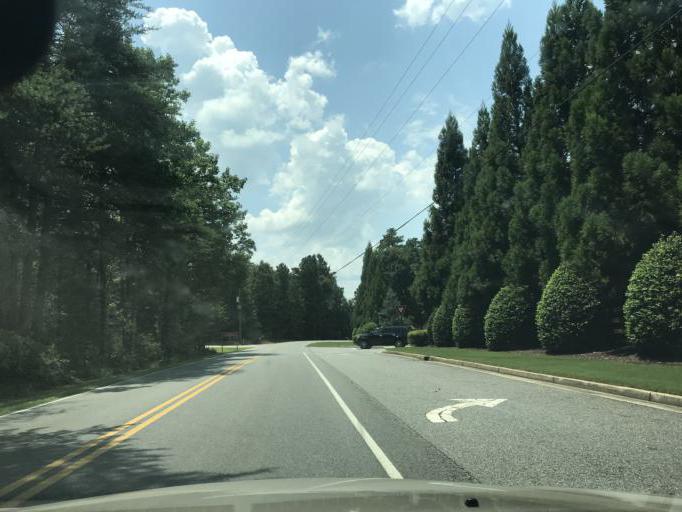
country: US
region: Georgia
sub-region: Forsyth County
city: Cumming
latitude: 34.2757
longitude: -84.1388
